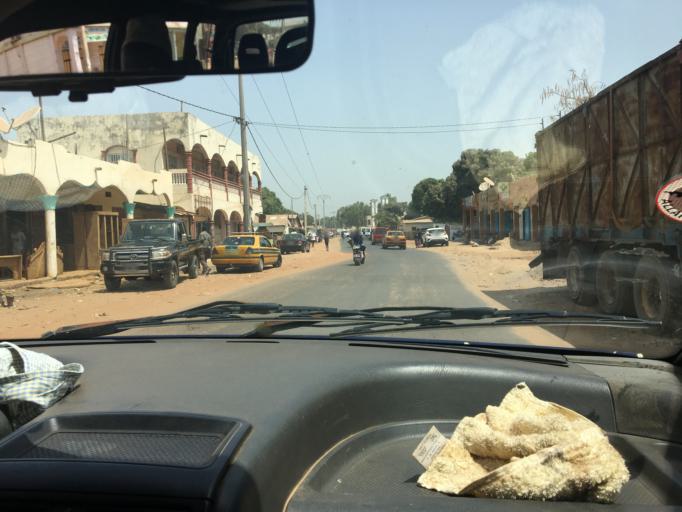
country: GM
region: Western
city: Abuko
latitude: 13.3946
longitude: -16.6739
